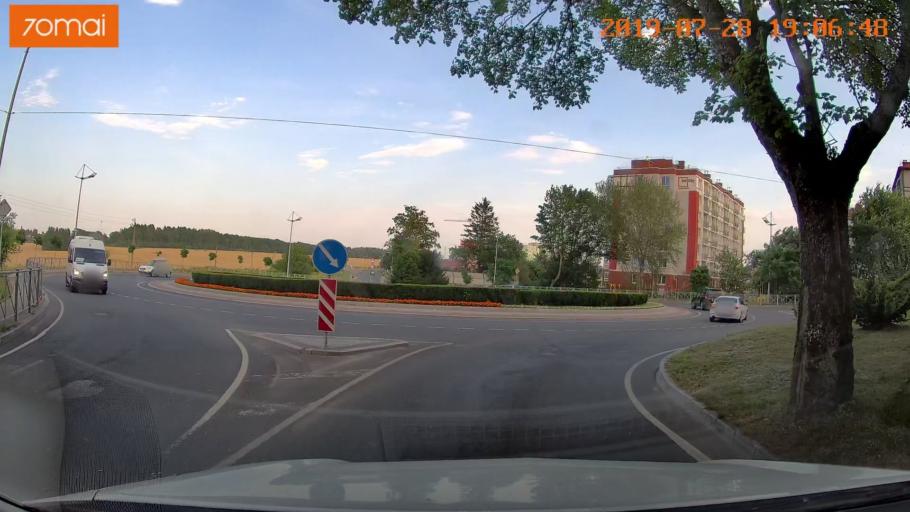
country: RU
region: Kaliningrad
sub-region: Gorod Svetlogorsk
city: Svetlogorsk
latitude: 54.9296
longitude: 20.1674
